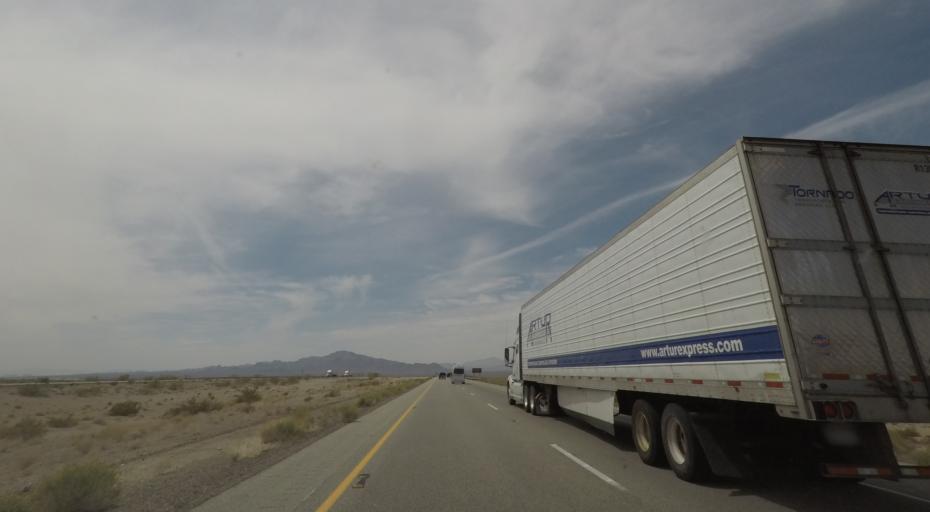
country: US
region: California
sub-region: San Bernardino County
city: Needles
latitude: 34.8139
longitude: -115.1790
